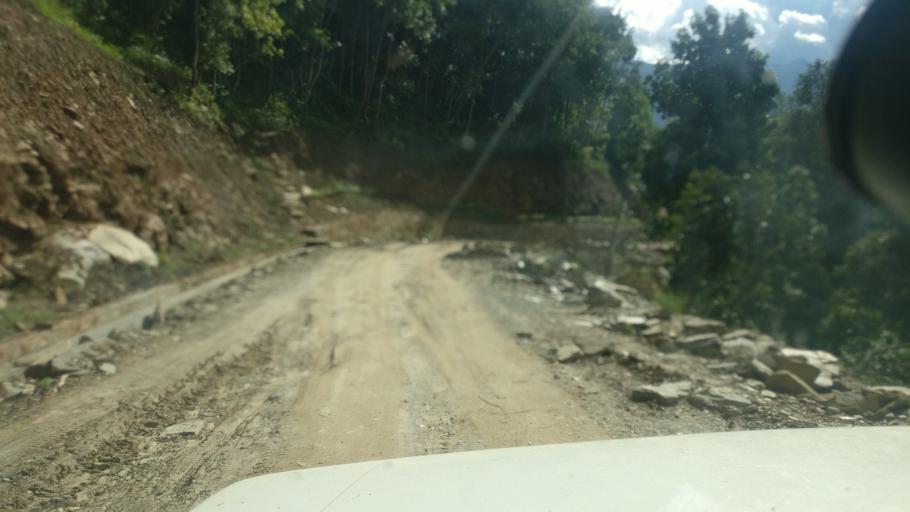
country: NP
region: Western Region
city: Baglung
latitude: 28.2670
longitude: 83.6470
